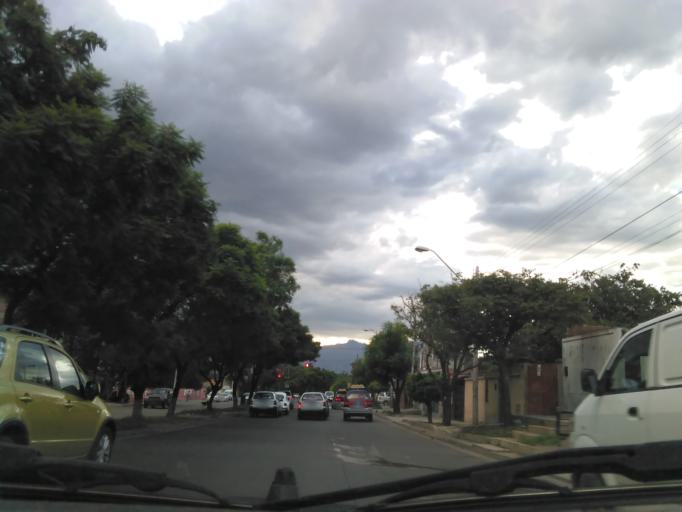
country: BO
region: Cochabamba
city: Cochabamba
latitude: -17.3651
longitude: -66.1615
